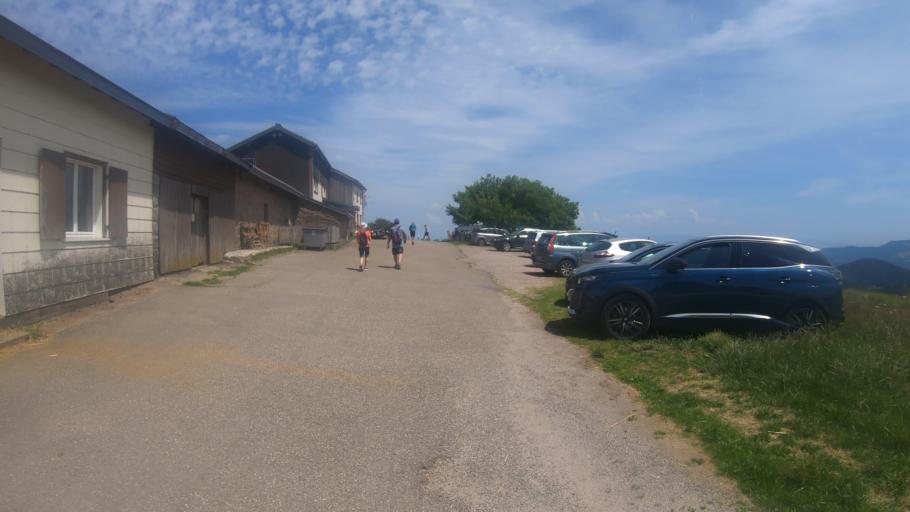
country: FR
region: Alsace
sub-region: Departement du Haut-Rhin
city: Metzeral
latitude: 48.0531
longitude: 7.0241
